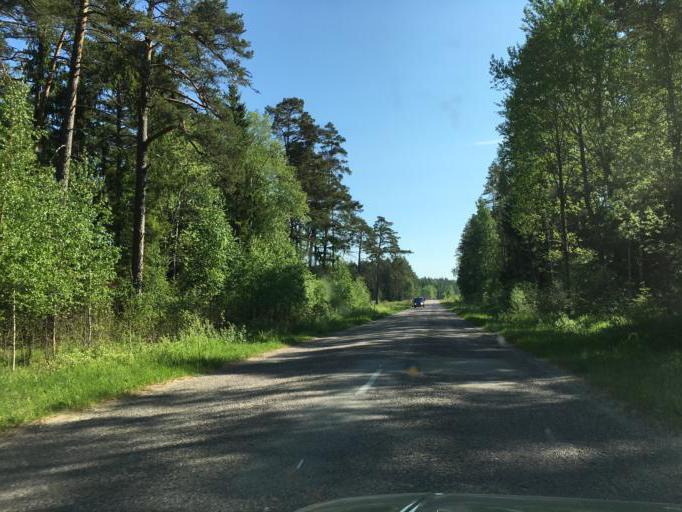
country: LV
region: Ventspils
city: Ventspils
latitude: 57.5115
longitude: 21.8618
